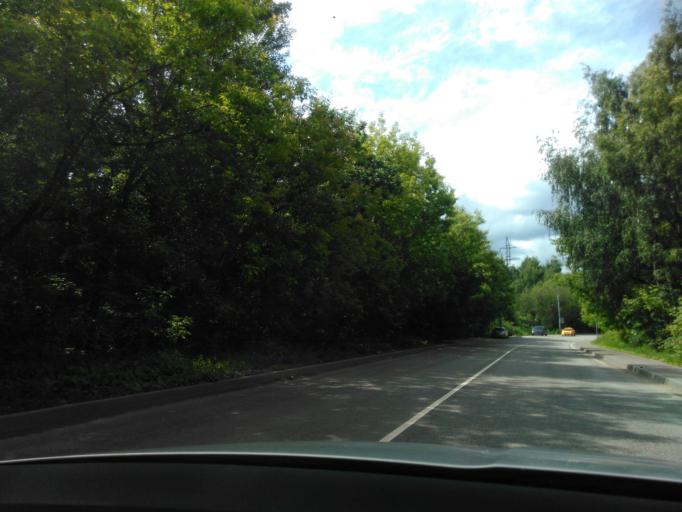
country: RU
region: Moskovskaya
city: Levoberezhnaya
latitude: 55.8784
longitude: 37.4742
